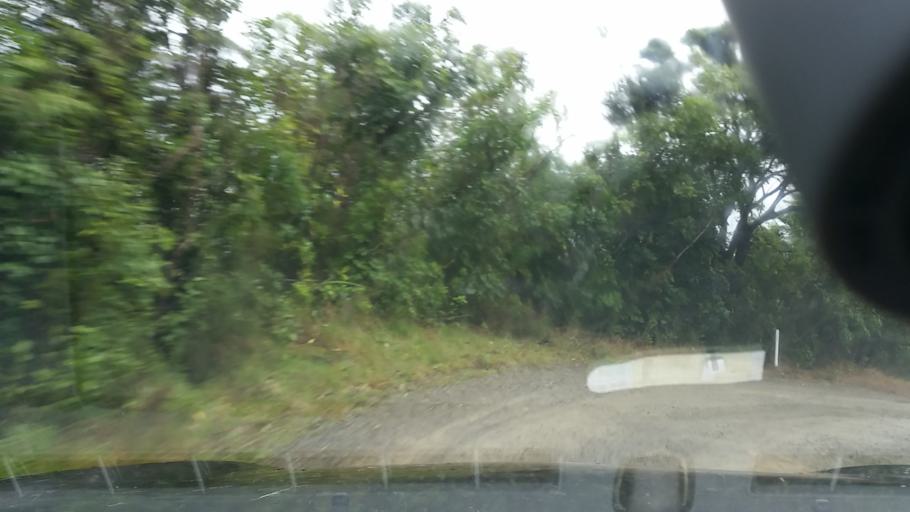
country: NZ
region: Marlborough
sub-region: Marlborough District
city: Picton
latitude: -41.3453
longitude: 174.0757
